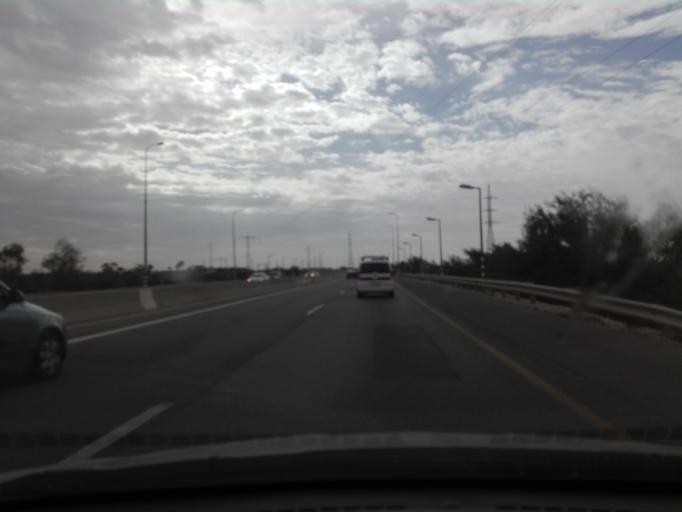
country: IL
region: Southern District
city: Lehavim
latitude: 31.3319
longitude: 34.7869
